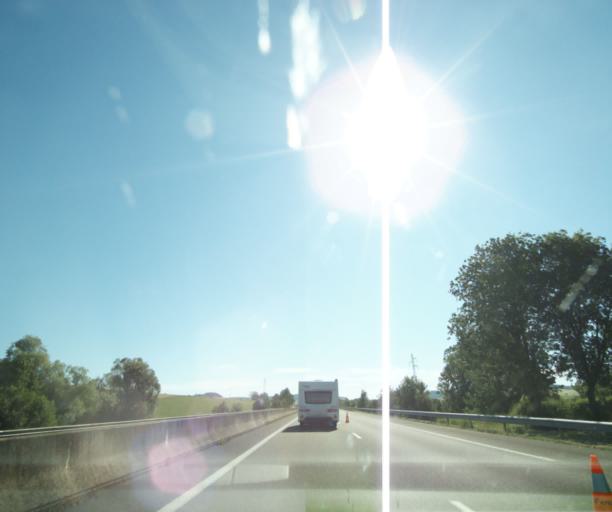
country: FR
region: Champagne-Ardenne
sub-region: Departement de la Haute-Marne
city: Nogent-le-Bas
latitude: 47.9533
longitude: 5.3651
